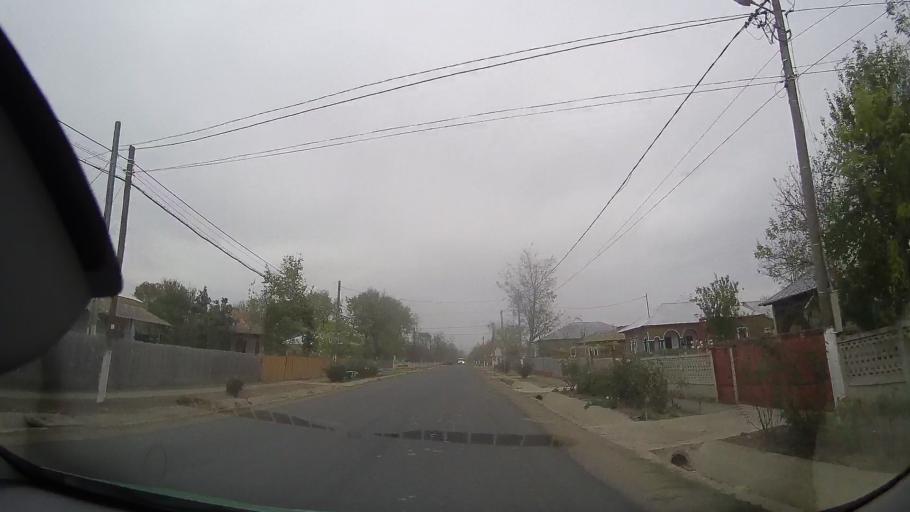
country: RO
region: Braila
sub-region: Comuna Rosiori
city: Rosiori
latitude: 44.8094
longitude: 27.3862
